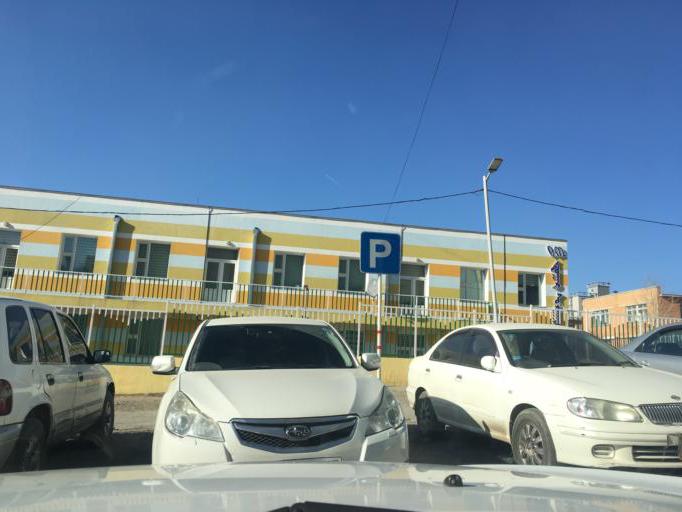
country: MN
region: Ulaanbaatar
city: Ulaanbaatar
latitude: 47.9202
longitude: 106.8645
